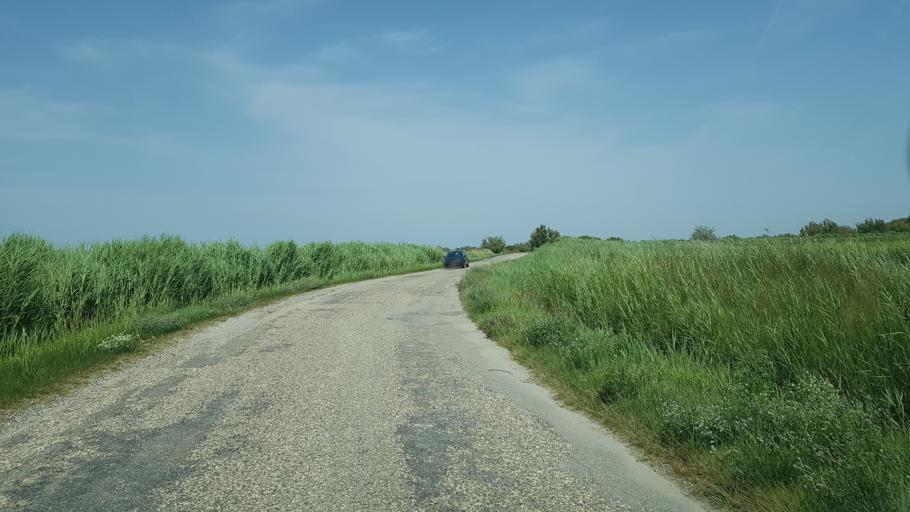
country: FR
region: Provence-Alpes-Cote d'Azur
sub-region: Departement des Bouches-du-Rhone
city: Arles
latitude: 43.5108
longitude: 4.6337
